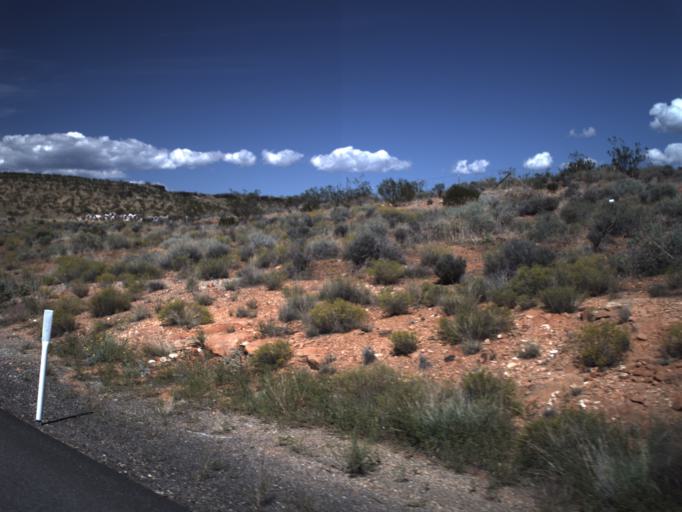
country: US
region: Utah
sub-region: Washington County
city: Santa Clara
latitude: 37.1667
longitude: -113.6142
